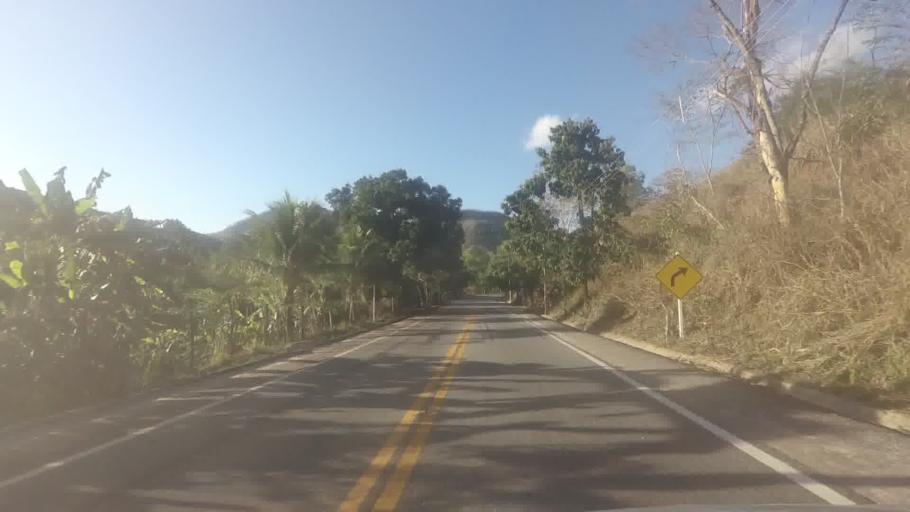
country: BR
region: Espirito Santo
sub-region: Cachoeiro De Itapemirim
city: Cachoeiro de Itapemirim
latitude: -20.8356
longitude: -41.2273
